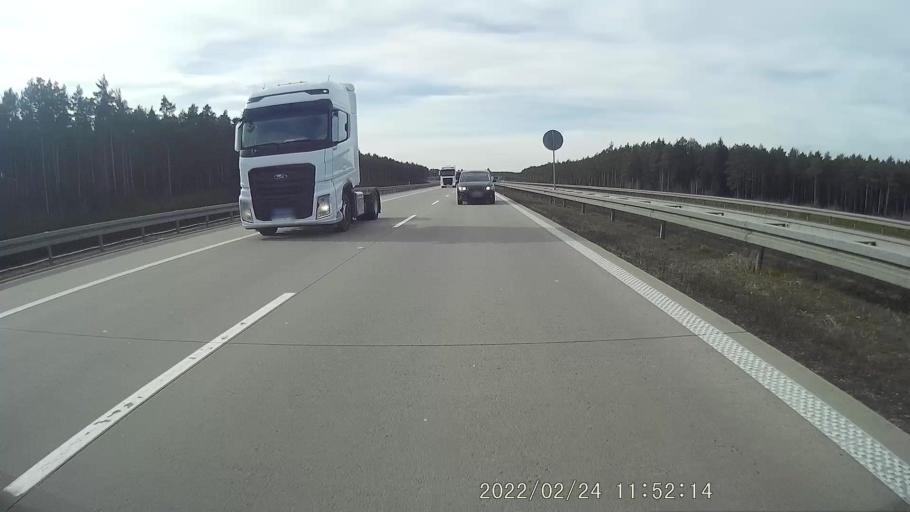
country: PL
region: Lower Silesian Voivodeship
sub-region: Powiat polkowicki
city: Radwanice
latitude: 51.6197
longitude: 15.9750
